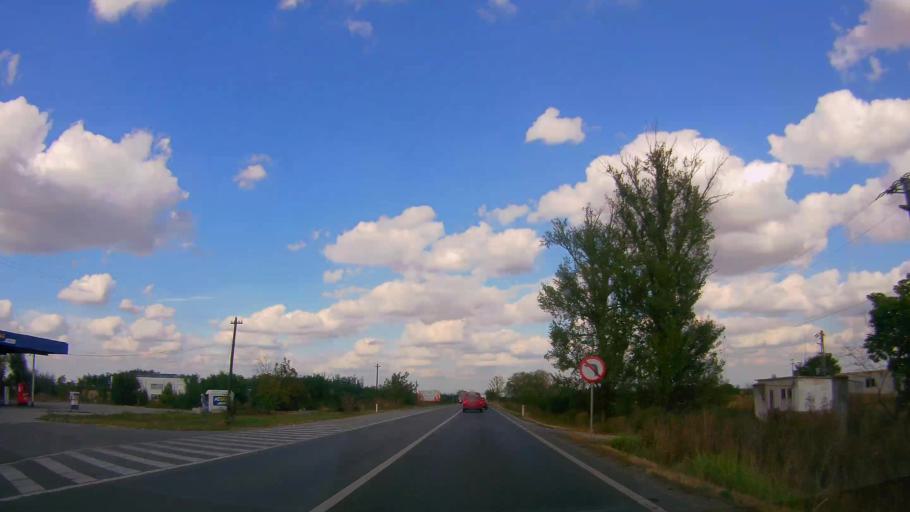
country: RO
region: Satu Mare
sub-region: Comuna Botiz
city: Botiz
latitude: 47.8156
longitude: 22.9293
